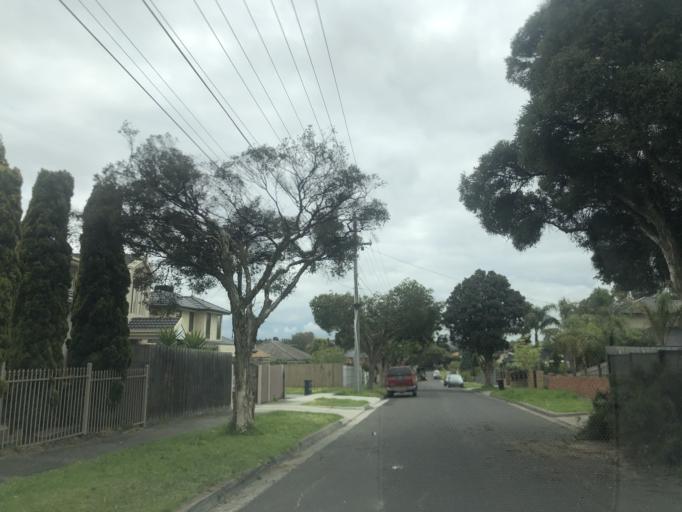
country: AU
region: Victoria
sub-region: Greater Dandenong
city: Dandenong North
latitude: -37.9672
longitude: 145.1994
